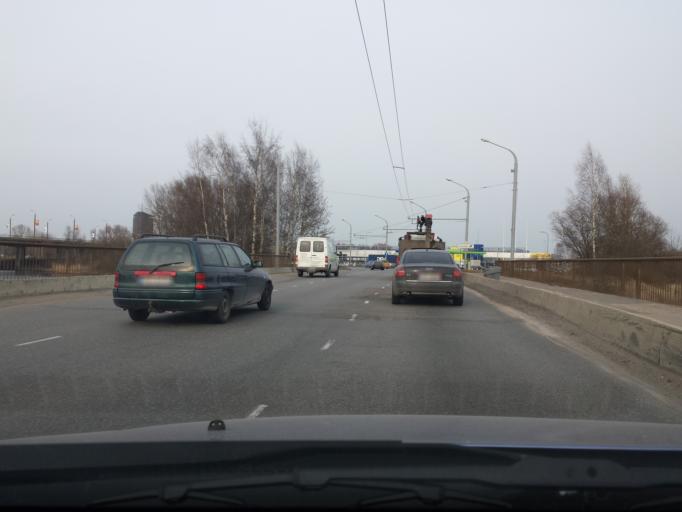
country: LV
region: Riga
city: Riga
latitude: 56.9235
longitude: 24.1085
